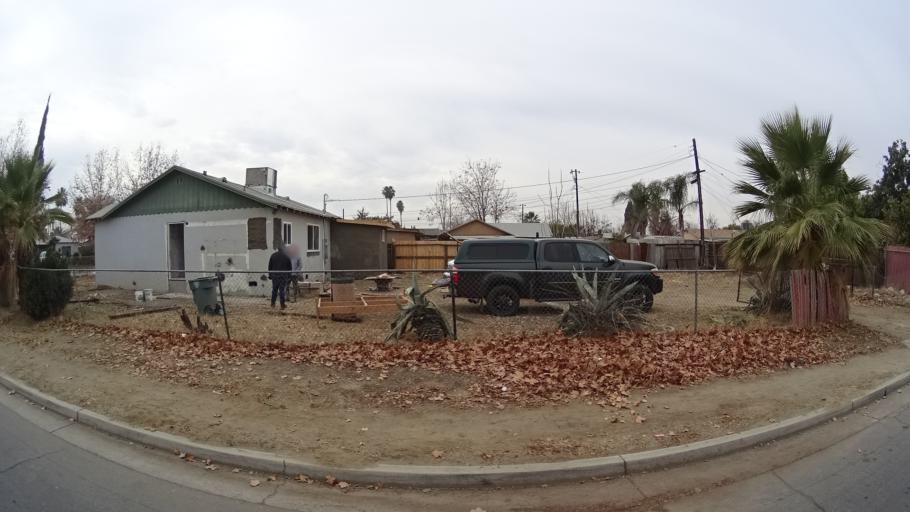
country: US
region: California
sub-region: Kern County
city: Bakersfield
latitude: 35.3552
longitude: -118.9992
